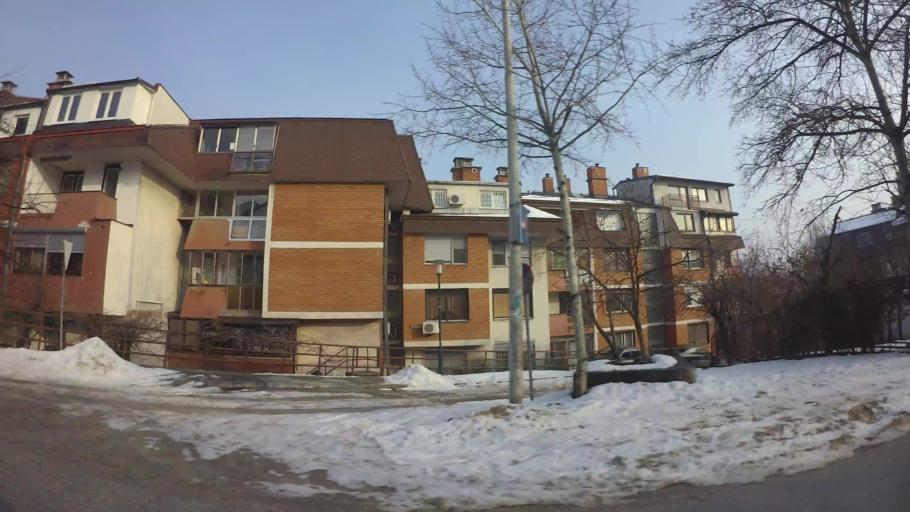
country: BA
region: Federation of Bosnia and Herzegovina
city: Kobilja Glava
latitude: 43.8691
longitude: 18.3999
